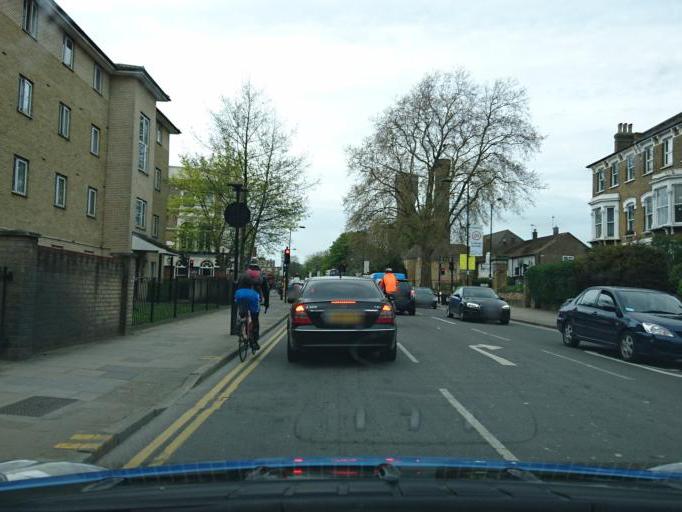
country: GB
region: England
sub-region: Greater London
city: Harringay
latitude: 51.5634
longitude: -0.0922
